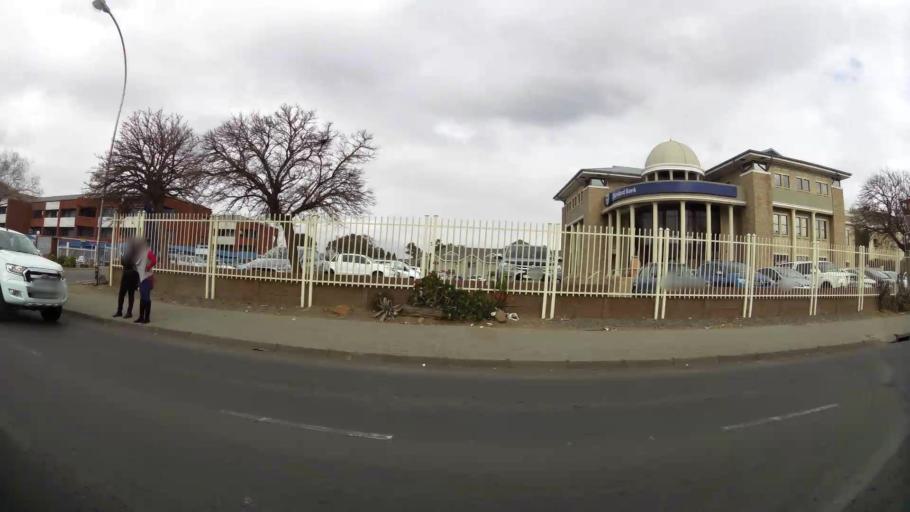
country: ZA
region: Orange Free State
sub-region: Mangaung Metropolitan Municipality
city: Bloemfontein
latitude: -29.1104
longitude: 26.2039
